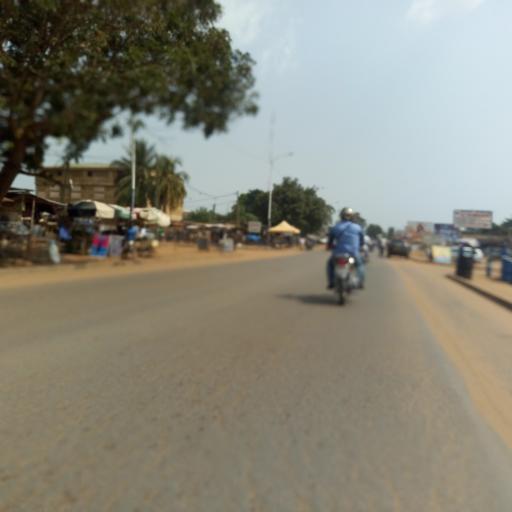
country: TG
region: Maritime
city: Lome
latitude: 6.1830
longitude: 1.1688
